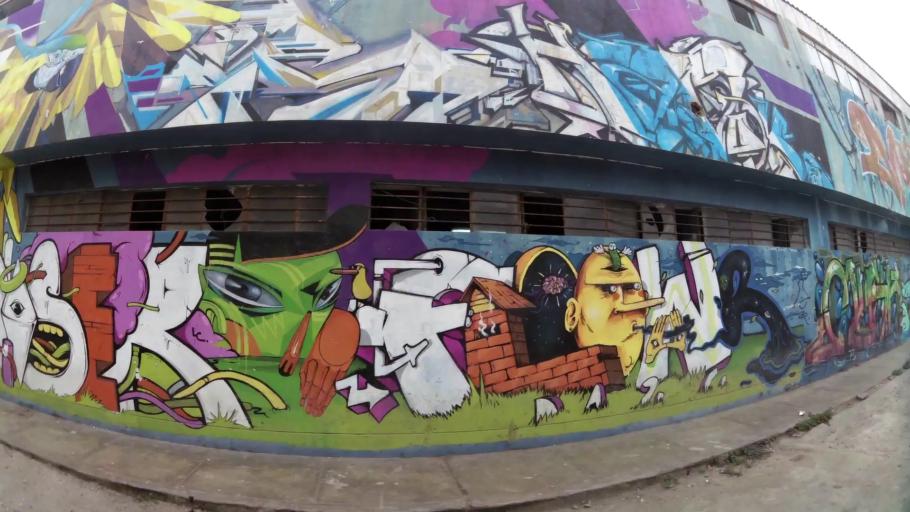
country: PE
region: Lima
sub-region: Lima
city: Surco
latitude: -12.1823
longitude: -77.0130
